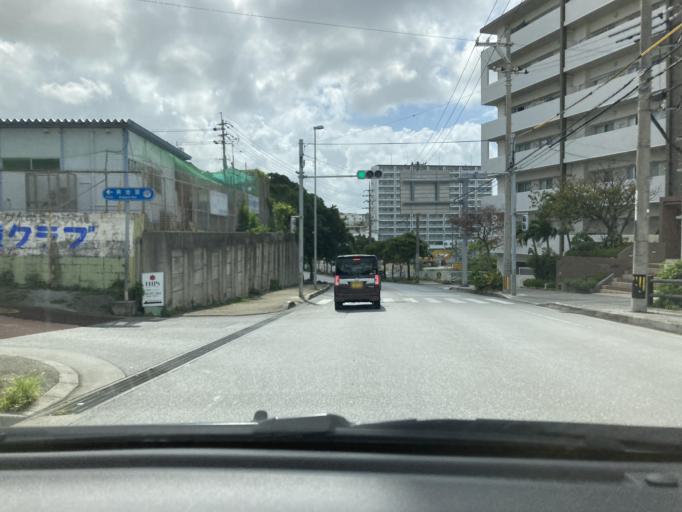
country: JP
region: Okinawa
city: Ginowan
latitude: 26.2658
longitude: 127.7339
